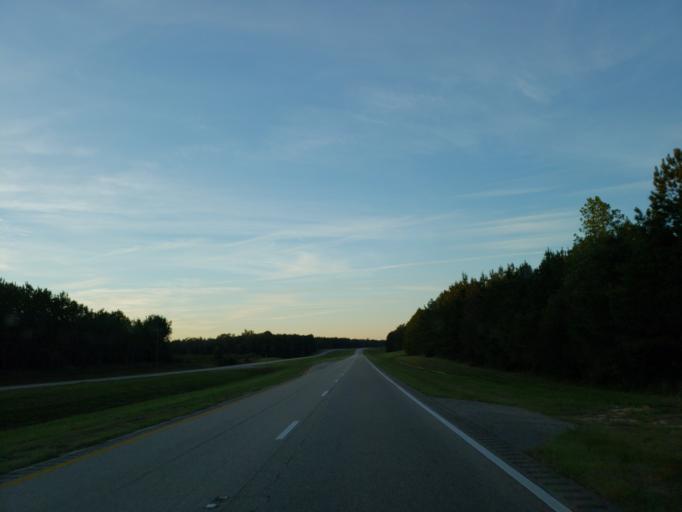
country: US
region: Mississippi
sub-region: Wayne County
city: Belmont
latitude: 31.4834
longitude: -88.4857
